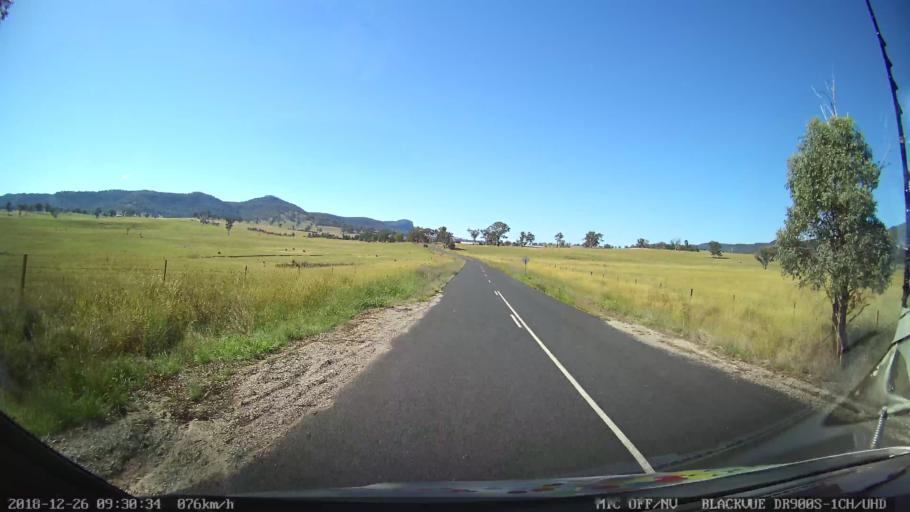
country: AU
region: New South Wales
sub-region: Mid-Western Regional
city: Kandos
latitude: -32.8644
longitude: 150.0287
